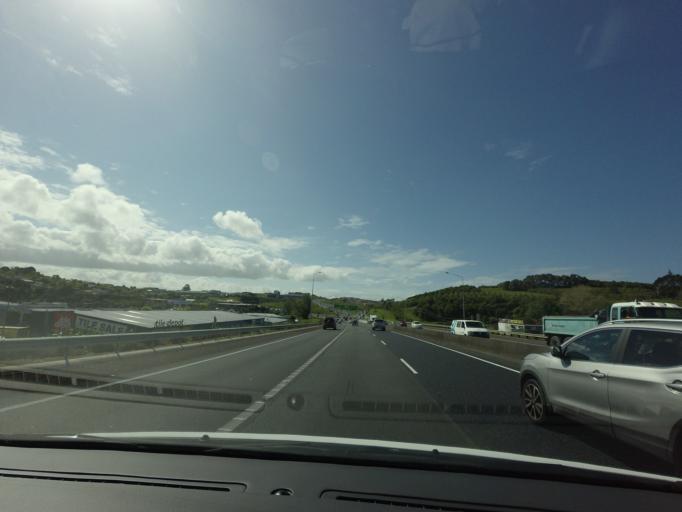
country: NZ
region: Auckland
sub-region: Auckland
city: Rothesay Bay
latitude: -36.7397
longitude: 174.7195
